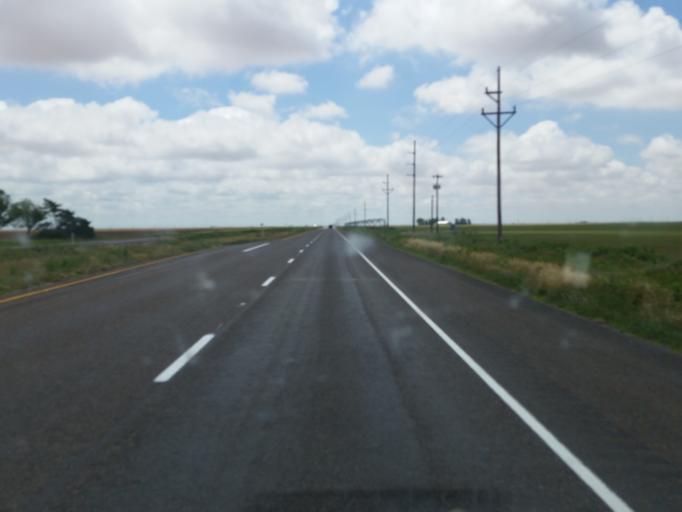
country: US
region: Texas
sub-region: Lubbock County
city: Slaton
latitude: 33.3986
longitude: -101.6109
